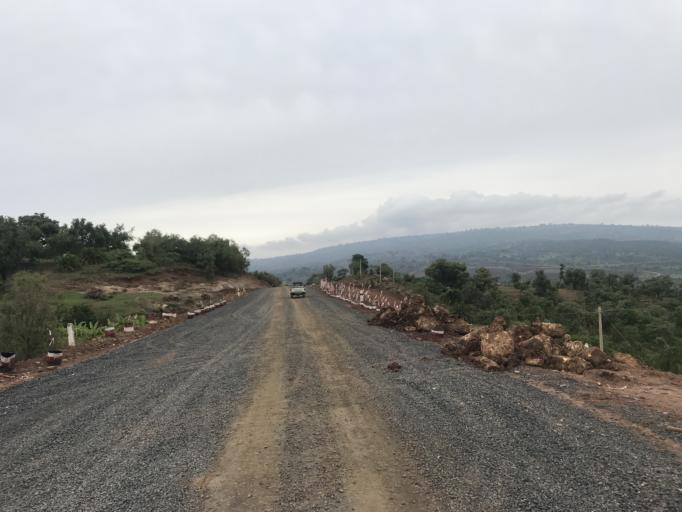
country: ET
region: Oromiya
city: Shambu
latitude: 10.0763
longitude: 36.8803
